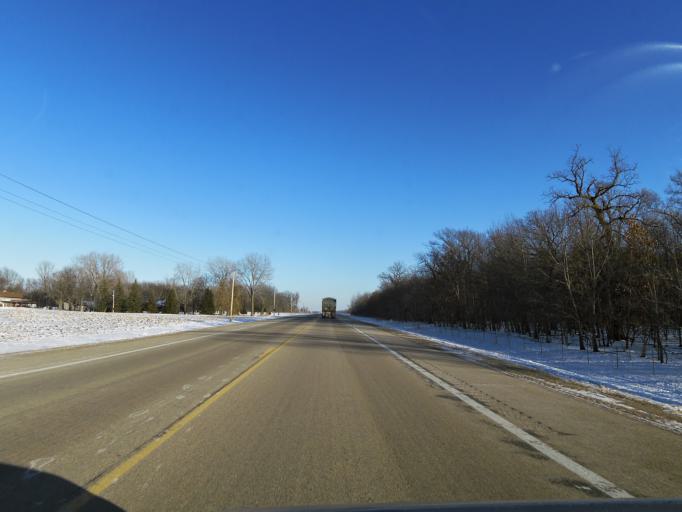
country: US
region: Minnesota
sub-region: Rice County
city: Lonsdale
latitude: 44.4860
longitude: -93.5090
